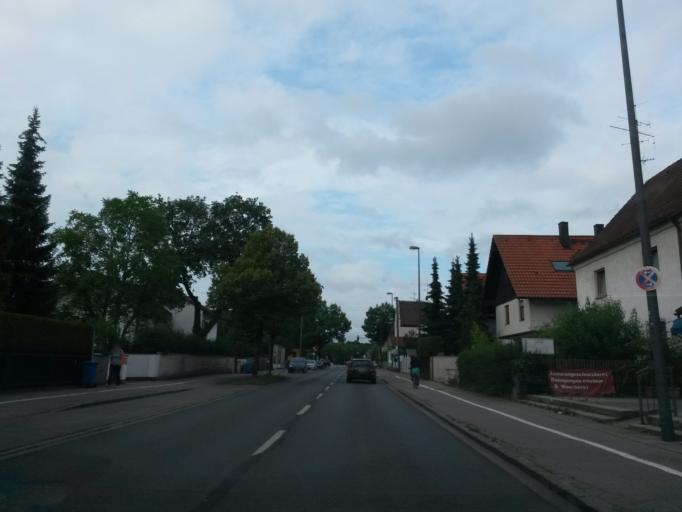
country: DE
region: Bavaria
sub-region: Upper Bavaria
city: Neubiberg
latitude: 48.1139
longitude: 11.6513
